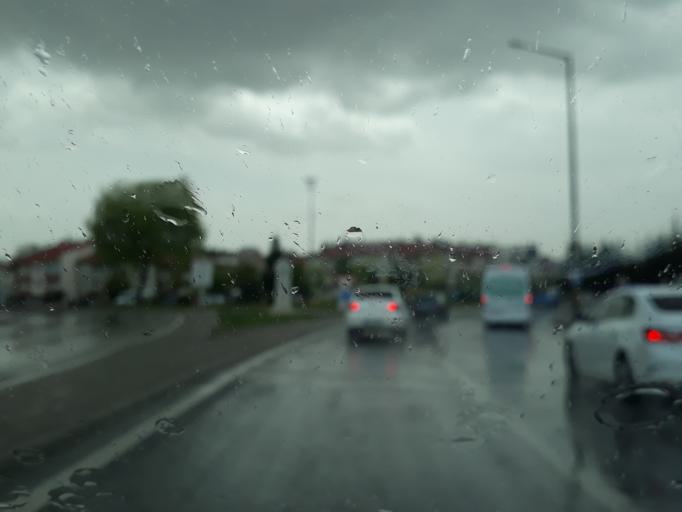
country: TR
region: Konya
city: Selcuklu
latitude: 37.9164
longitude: 32.4926
